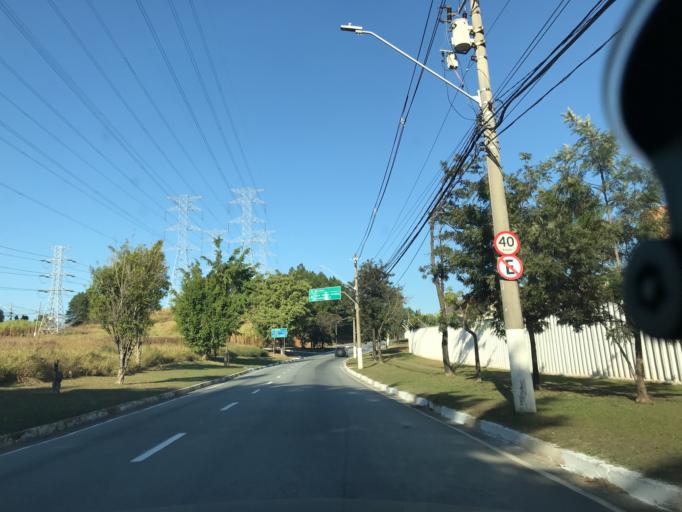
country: BR
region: Sao Paulo
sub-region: Barueri
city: Barueri
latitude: -23.4647
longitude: -46.8728
